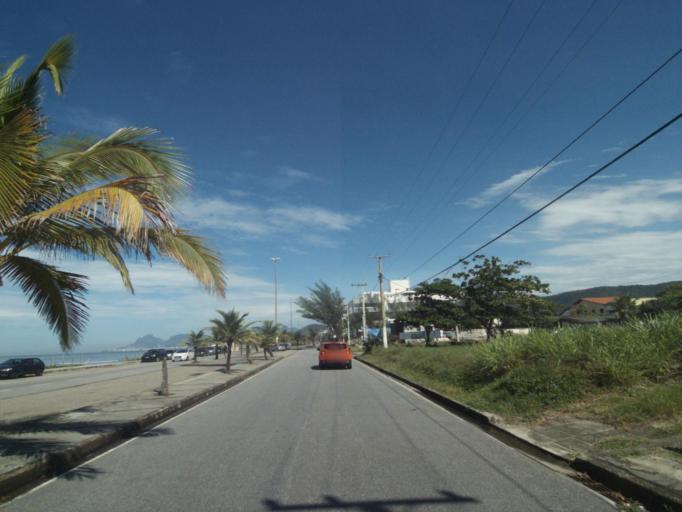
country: BR
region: Rio de Janeiro
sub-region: Niteroi
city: Niteroi
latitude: -22.9554
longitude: -43.0761
